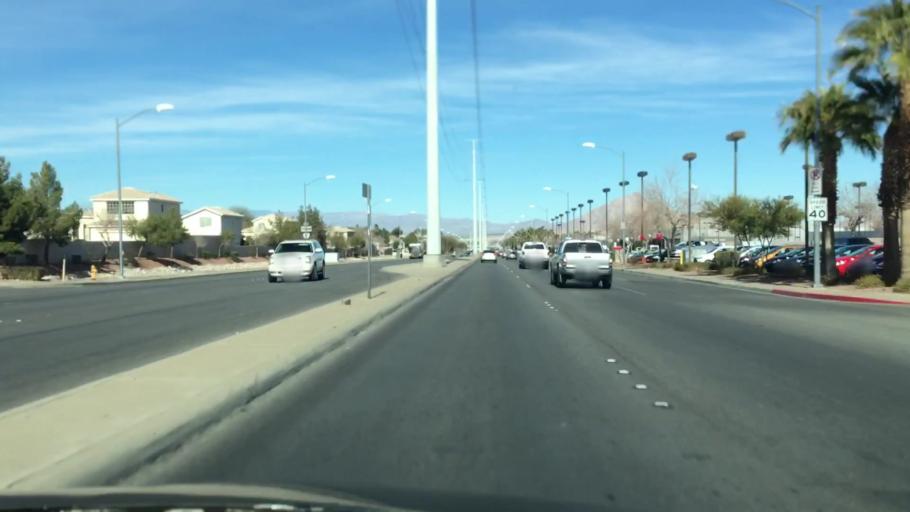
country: US
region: Nevada
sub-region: Clark County
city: Henderson
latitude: 36.0461
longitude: -115.0287
